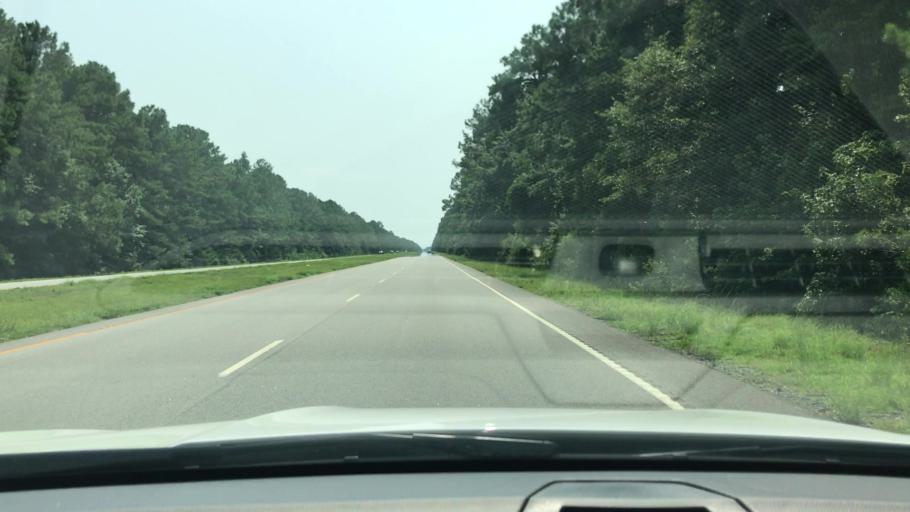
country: US
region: South Carolina
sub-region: Charleston County
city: Awendaw
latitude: 33.1613
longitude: -79.4260
